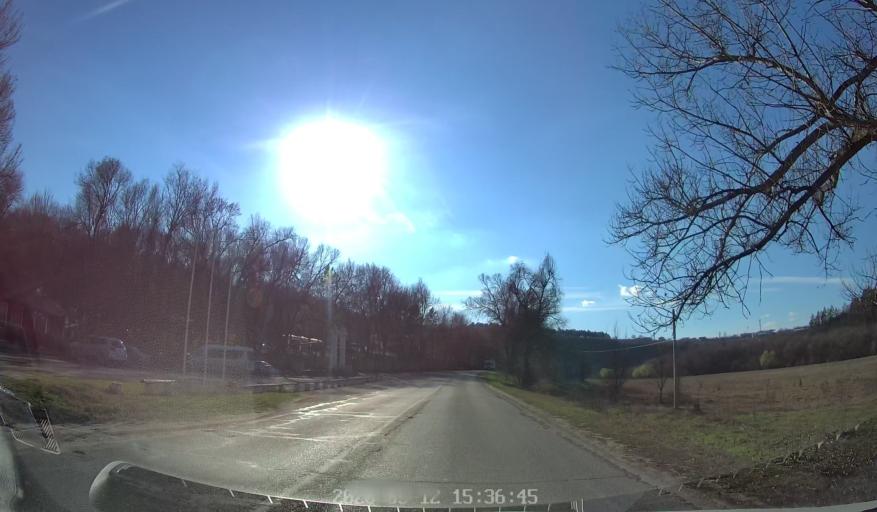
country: MD
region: Chisinau
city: Ciorescu
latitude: 47.1303
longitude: 28.9194
